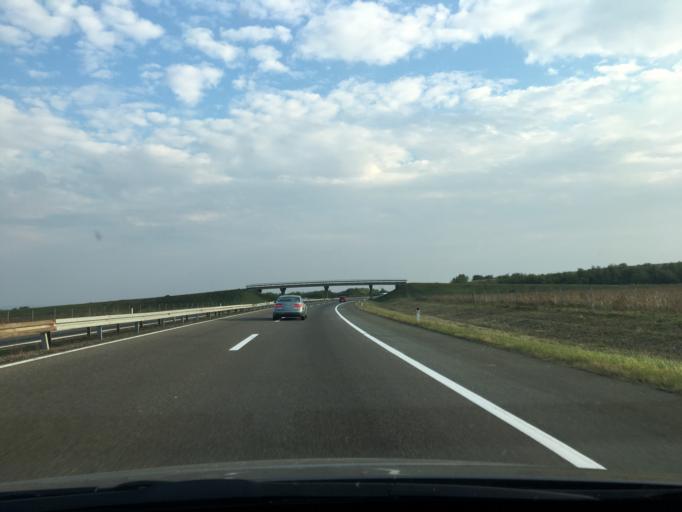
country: RS
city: Lugavcina
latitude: 44.5054
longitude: 21.0213
